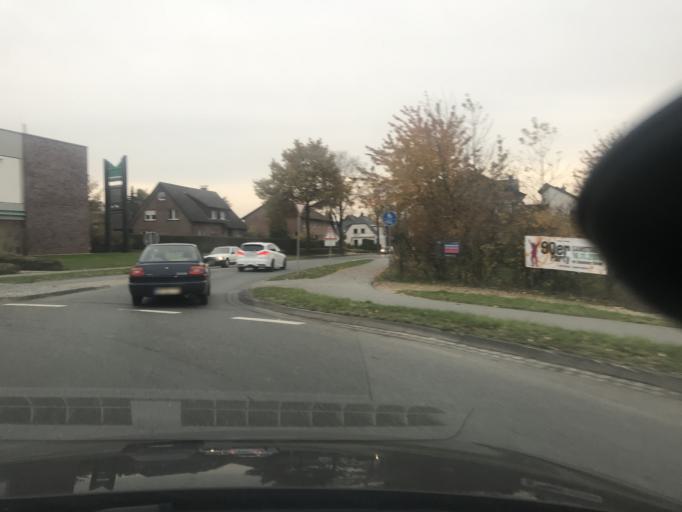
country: DE
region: North Rhine-Westphalia
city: Oelde
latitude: 51.8125
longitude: 8.1357
